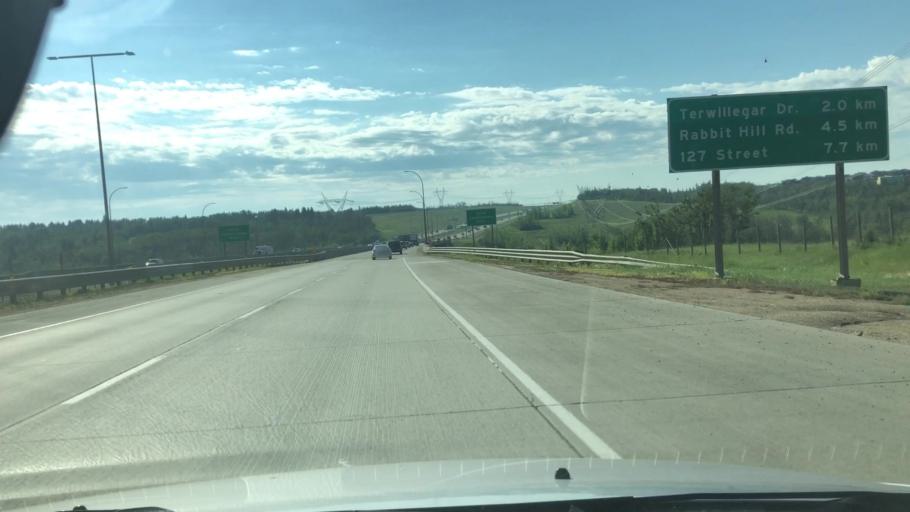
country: CA
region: Alberta
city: Devon
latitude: 53.4596
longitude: -113.6177
